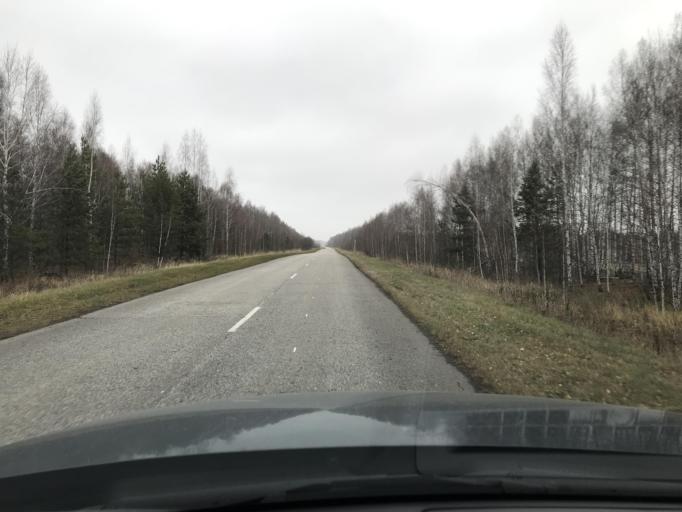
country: RU
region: Penza
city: Zemetchino
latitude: 53.6848
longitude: 42.6355
